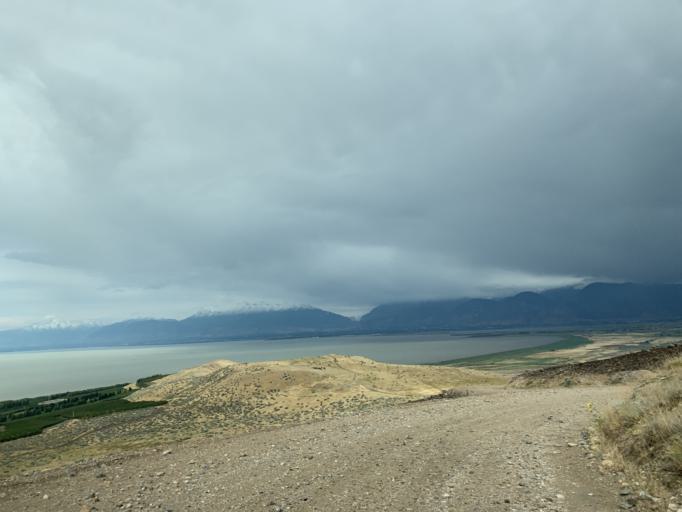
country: US
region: Utah
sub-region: Utah County
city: West Mountain
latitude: 40.1194
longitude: -111.8198
